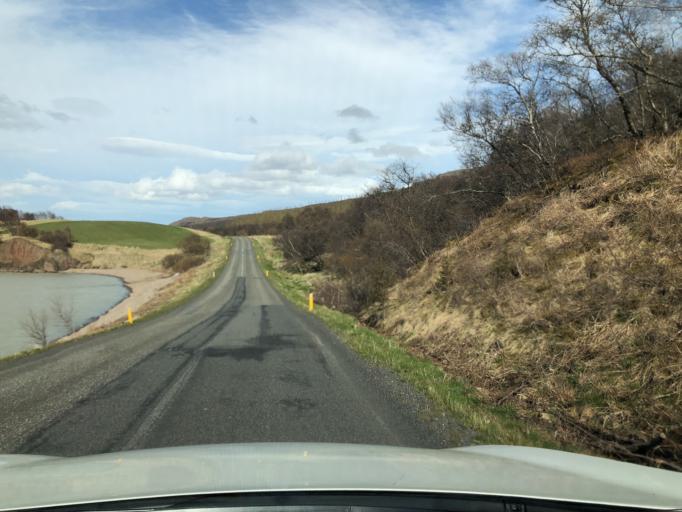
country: IS
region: East
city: Egilsstadir
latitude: 65.1037
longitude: -14.7273
